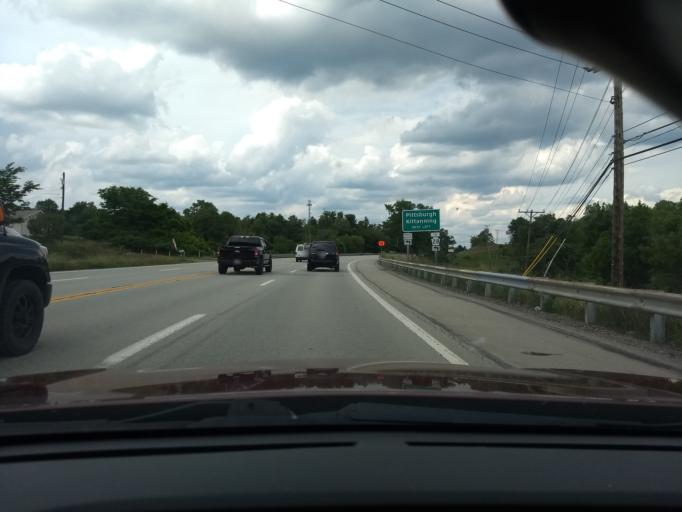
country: US
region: Pennsylvania
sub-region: Armstrong County
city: Freeport
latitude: 40.6606
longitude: -79.7076
